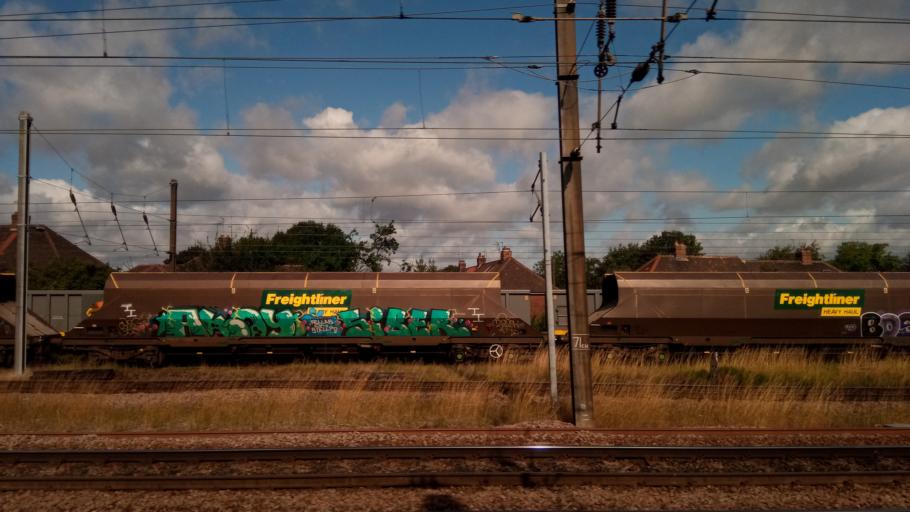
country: GB
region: England
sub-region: City of York
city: York
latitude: 53.9514
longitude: -1.1030
